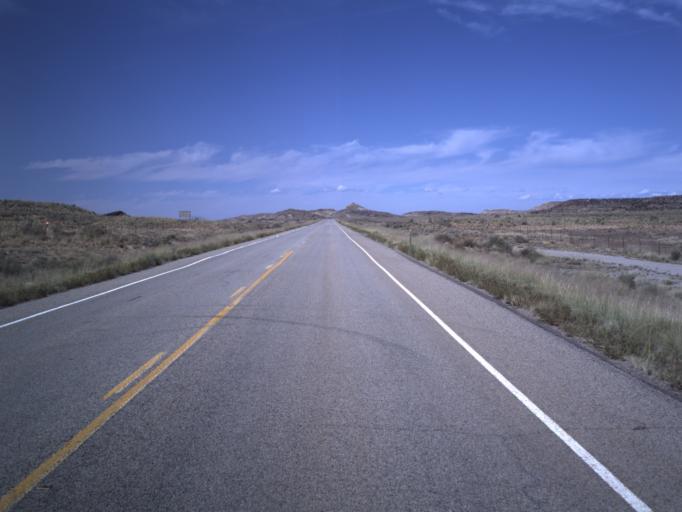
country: US
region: Colorado
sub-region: Montezuma County
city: Towaoc
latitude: 37.1670
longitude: -109.0805
